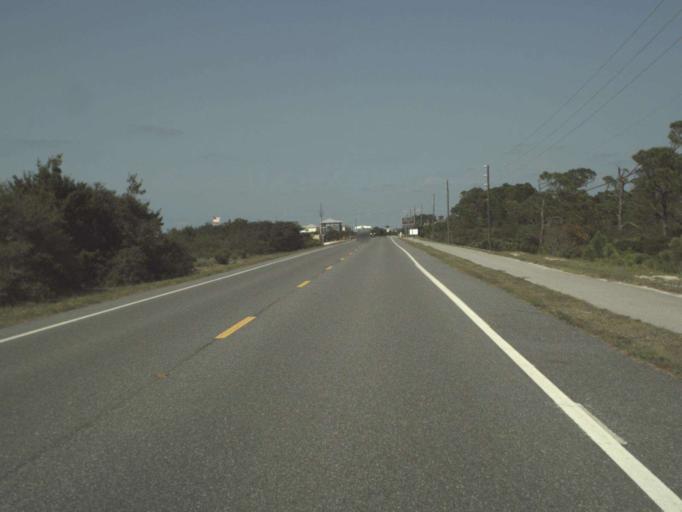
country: US
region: Florida
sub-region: Gulf County
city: Port Saint Joe
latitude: 29.7252
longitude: -85.3883
